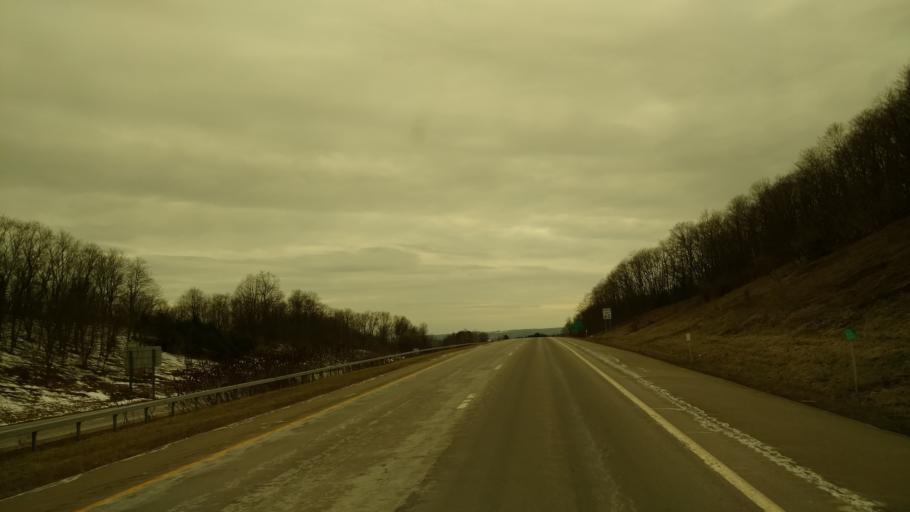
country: US
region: New York
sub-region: Chautauqua County
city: Jamestown
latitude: 42.1209
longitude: -79.2472
